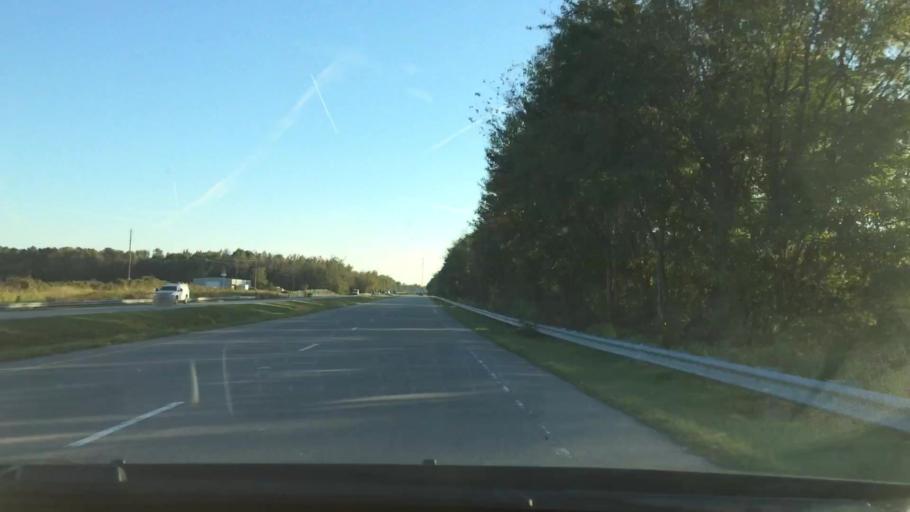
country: US
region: North Carolina
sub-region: Pitt County
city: Grifton
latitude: 35.3907
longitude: -77.4465
